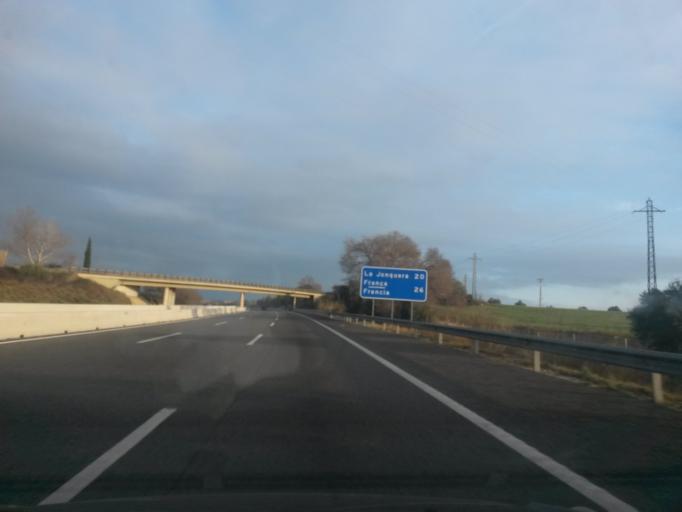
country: ES
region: Catalonia
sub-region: Provincia de Girona
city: Vilafant
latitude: 42.2534
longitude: 2.9441
